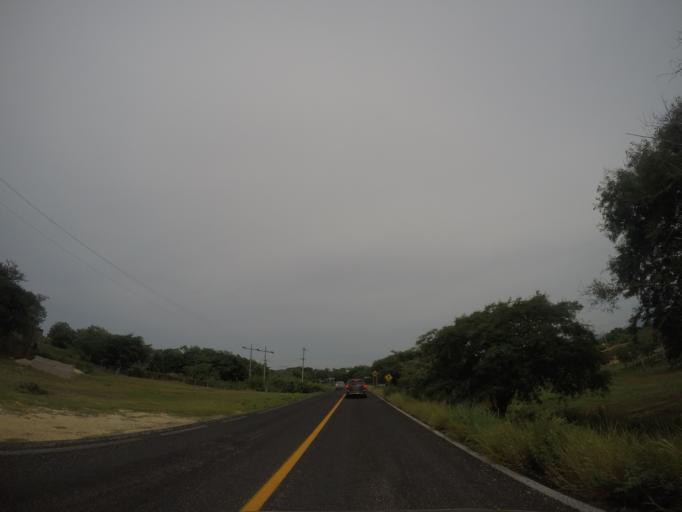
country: MX
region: Oaxaca
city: San Pedro Mixtepec
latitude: 15.9505
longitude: -97.2835
